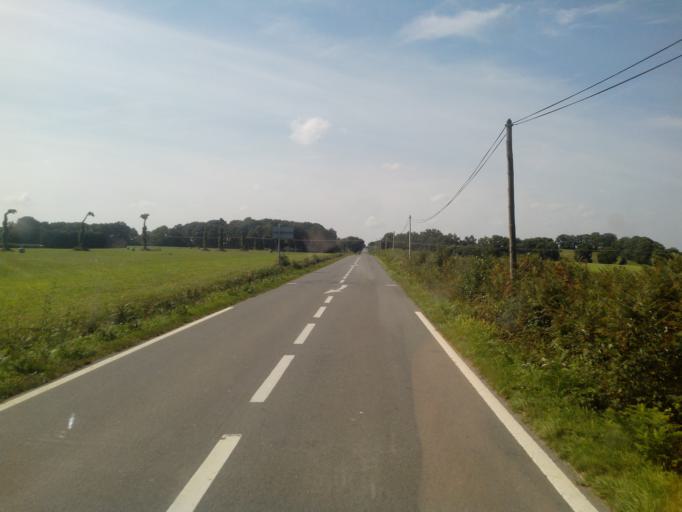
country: FR
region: Brittany
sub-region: Departement d'Ille-et-Vilaine
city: Gael
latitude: 48.1292
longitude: -2.2348
